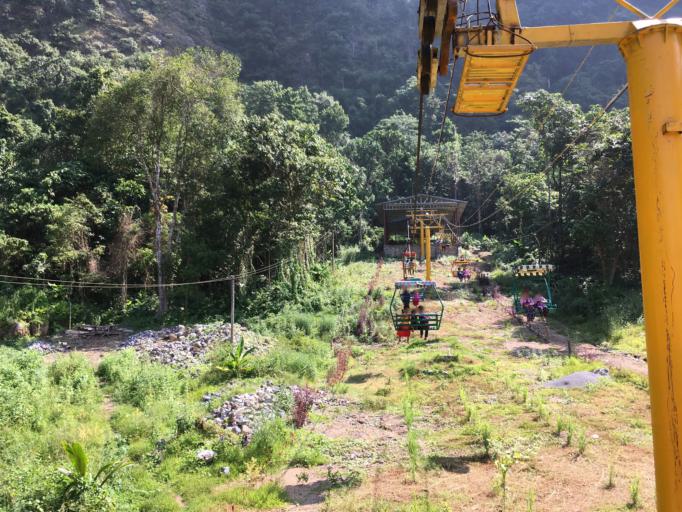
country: MM
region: Kayin
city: Hpa-an
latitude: 16.8096
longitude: 97.6754
